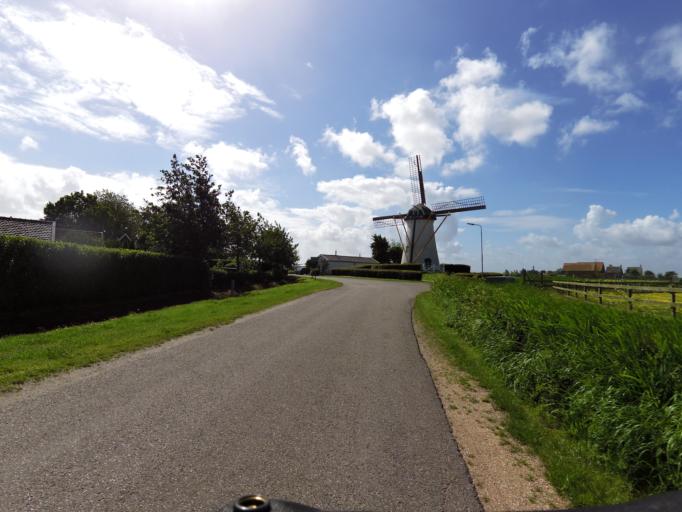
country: NL
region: Zeeland
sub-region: Schouwen-Duiveland
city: Bruinisse
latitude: 51.6882
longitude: 3.9870
